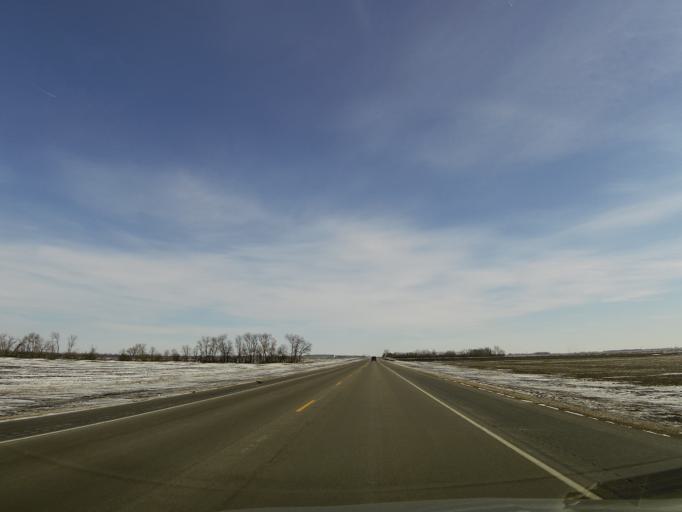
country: US
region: North Dakota
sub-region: Walsh County
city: Grafton
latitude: 48.4127
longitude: -97.3571
